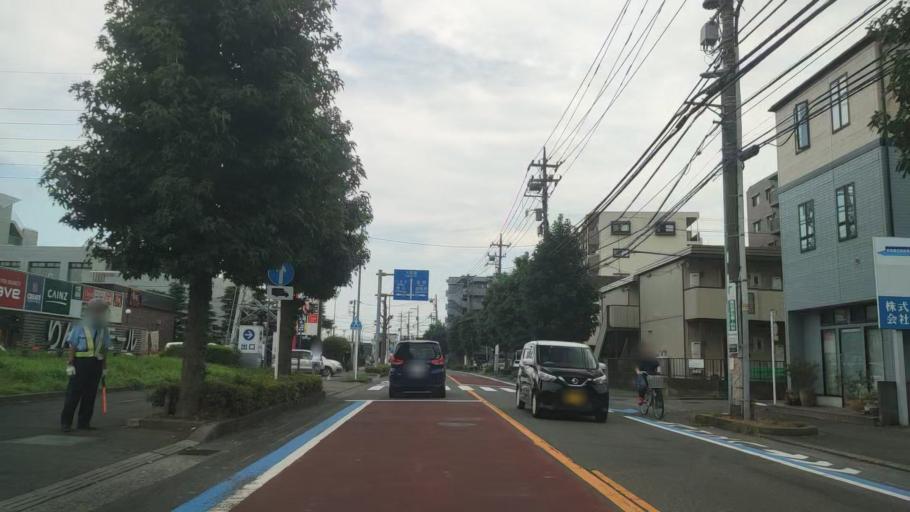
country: JP
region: Kanagawa
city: Minami-rinkan
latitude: 35.5029
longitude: 139.4494
